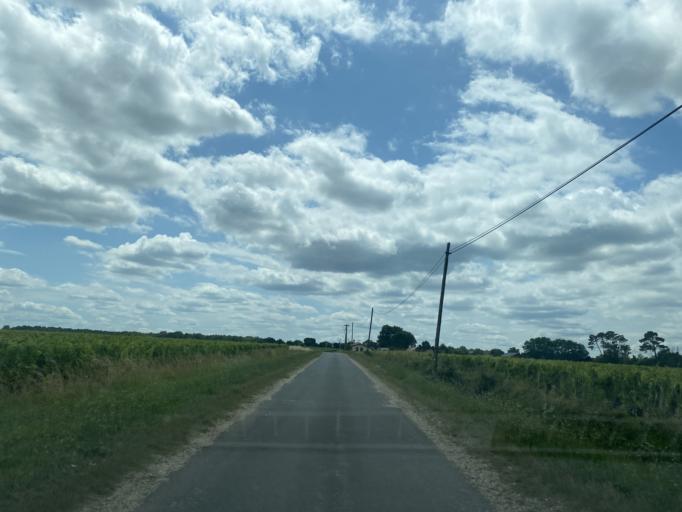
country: FR
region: Aquitaine
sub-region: Departement de la Gironde
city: Soussans
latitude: 45.0616
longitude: -0.6831
